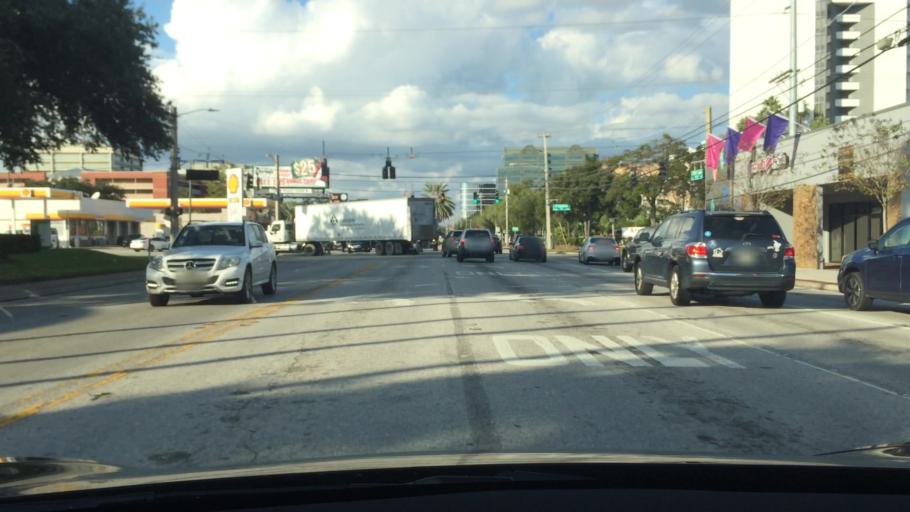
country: US
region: Florida
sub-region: Hillsborough County
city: Tampa
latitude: 27.9517
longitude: -82.5241
